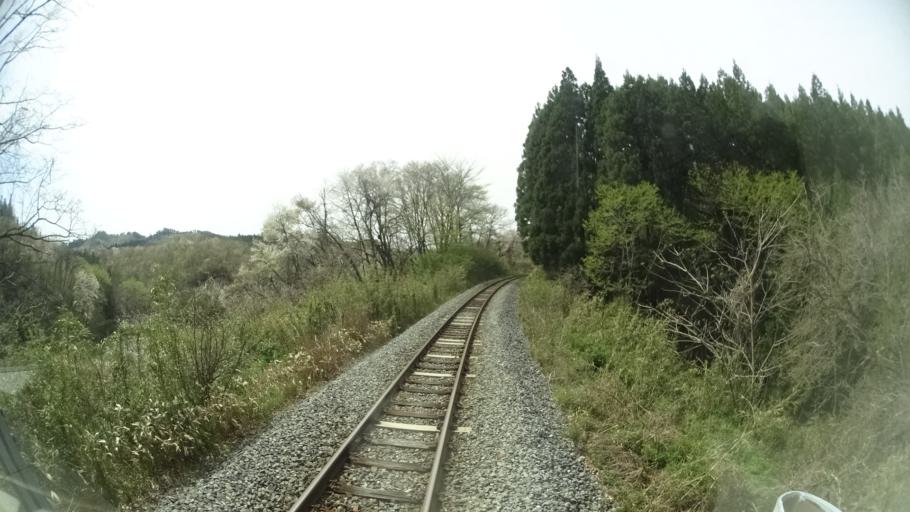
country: JP
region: Iwate
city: Ichinoseki
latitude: 38.9845
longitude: 141.3316
